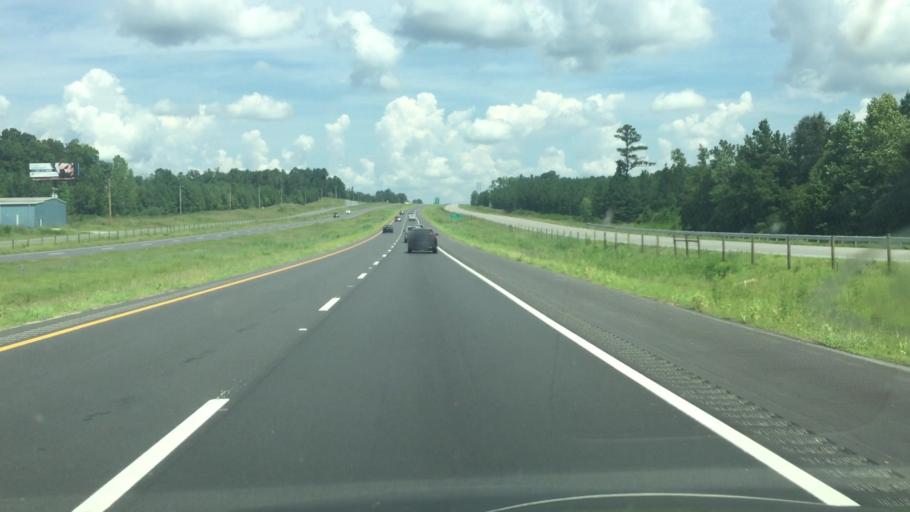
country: US
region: North Carolina
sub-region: Richmond County
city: Ellerbe
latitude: 35.0262
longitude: -79.7695
